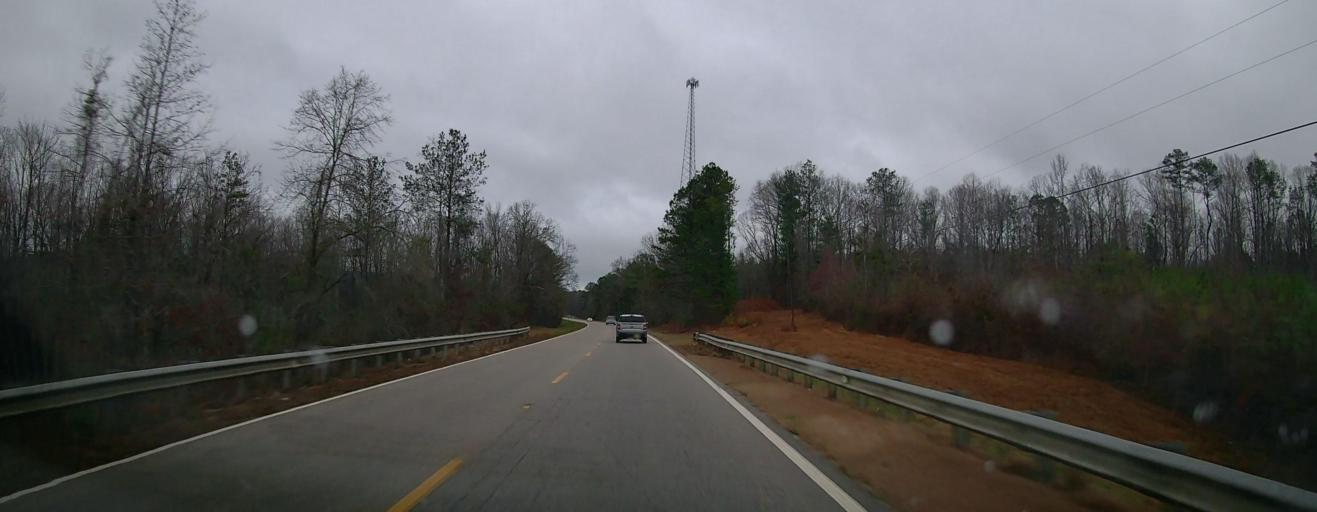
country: US
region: Alabama
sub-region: Bibb County
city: Centreville
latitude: 32.8868
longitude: -86.9828
